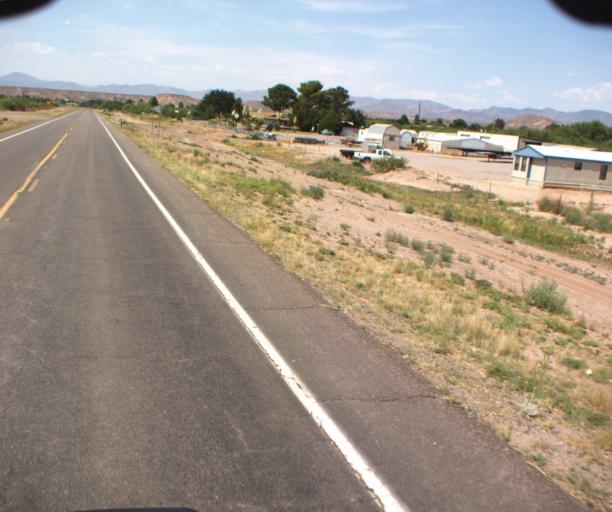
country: US
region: Arizona
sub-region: Greenlee County
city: Clifton
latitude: 32.9049
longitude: -109.1970
